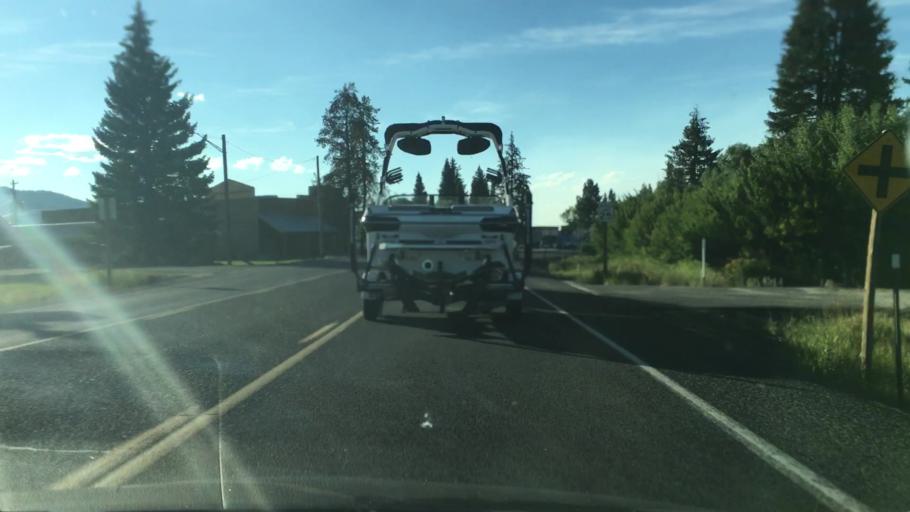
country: US
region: Idaho
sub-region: Valley County
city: McCall
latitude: 44.7298
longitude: -116.0775
